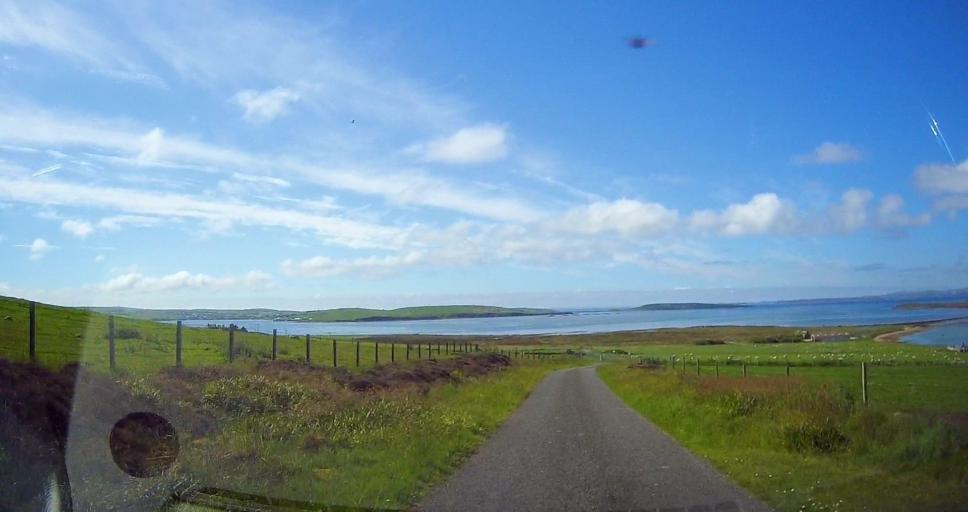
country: GB
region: Scotland
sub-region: Orkney Islands
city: Orkney
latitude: 58.8542
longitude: -2.9509
